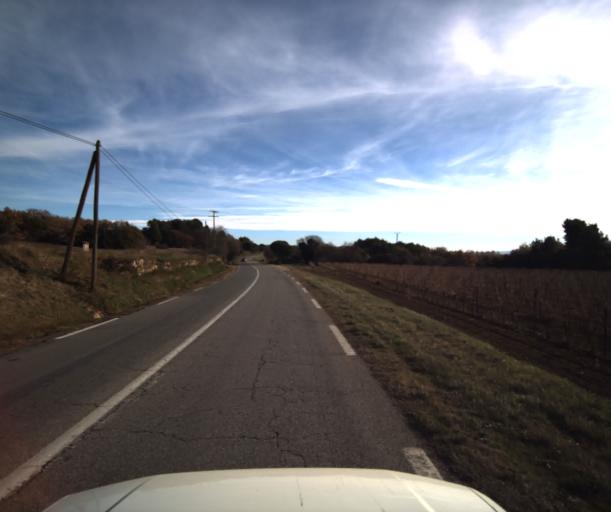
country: FR
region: Provence-Alpes-Cote d'Azur
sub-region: Departement du Vaucluse
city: Pertuis
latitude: 43.6983
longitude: 5.4680
